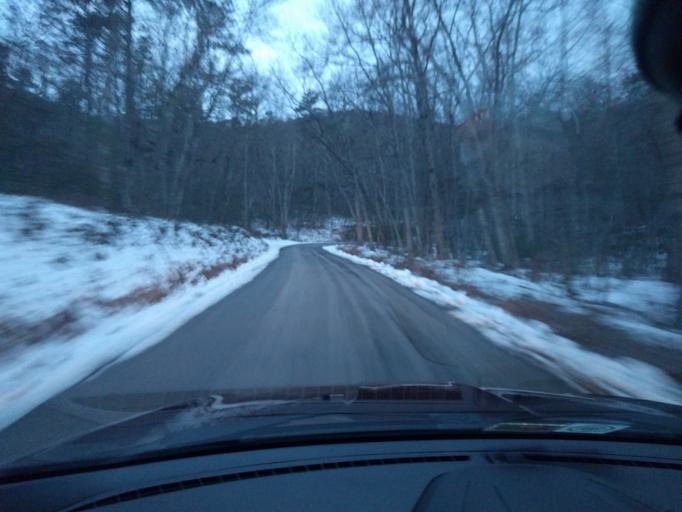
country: US
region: Virginia
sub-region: Alleghany County
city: Clifton Forge
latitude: 37.8649
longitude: -79.8813
